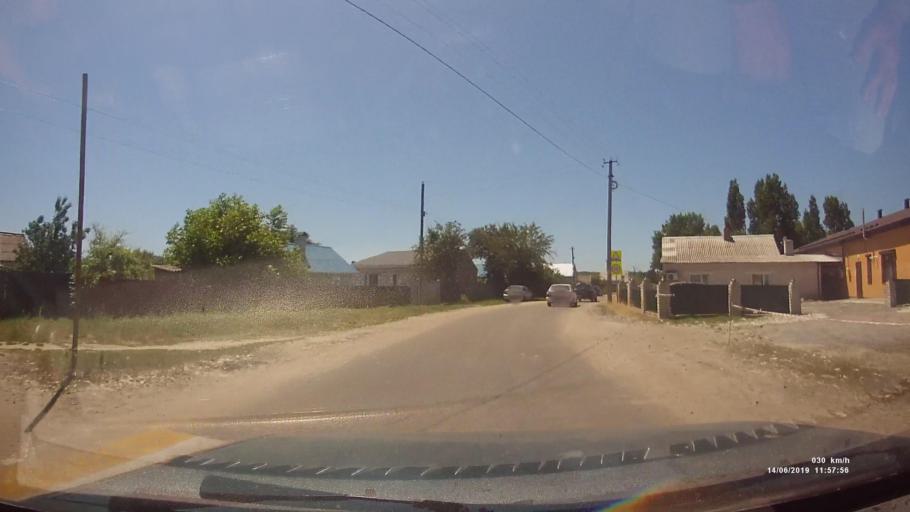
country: RU
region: Rostov
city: Kazanskaya
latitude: 49.7977
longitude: 41.1447
